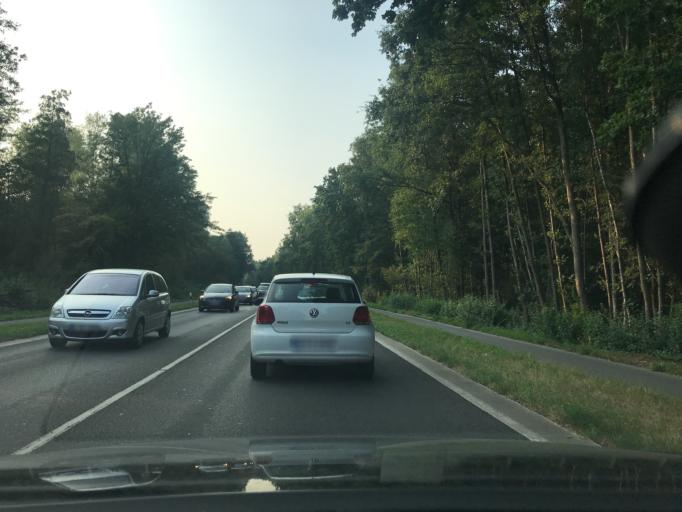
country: DE
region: North Rhine-Westphalia
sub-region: Regierungsbezirk Dusseldorf
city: Erkrath
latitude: 51.2077
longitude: 6.8788
